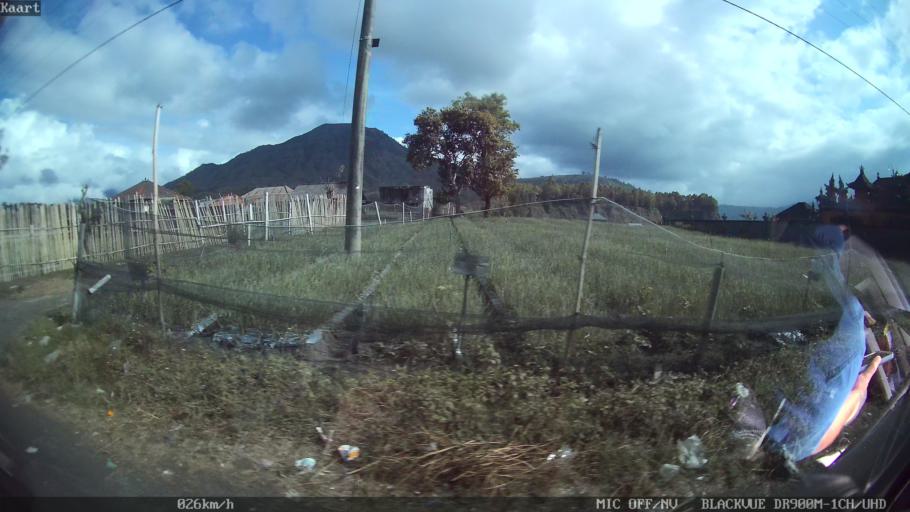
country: ID
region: Bali
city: Banjar Trunyan
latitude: -8.2150
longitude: 115.3742
